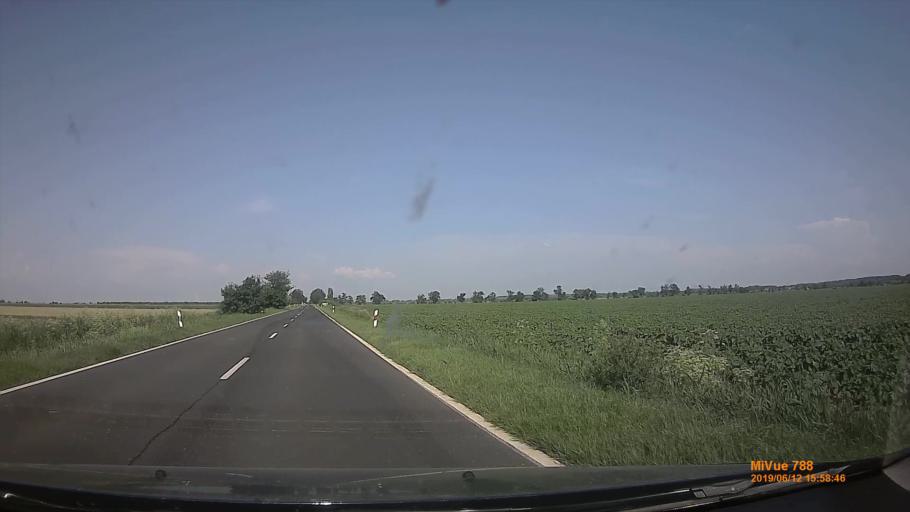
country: HU
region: Csongrad
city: Apatfalva
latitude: 46.1653
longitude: 20.6511
